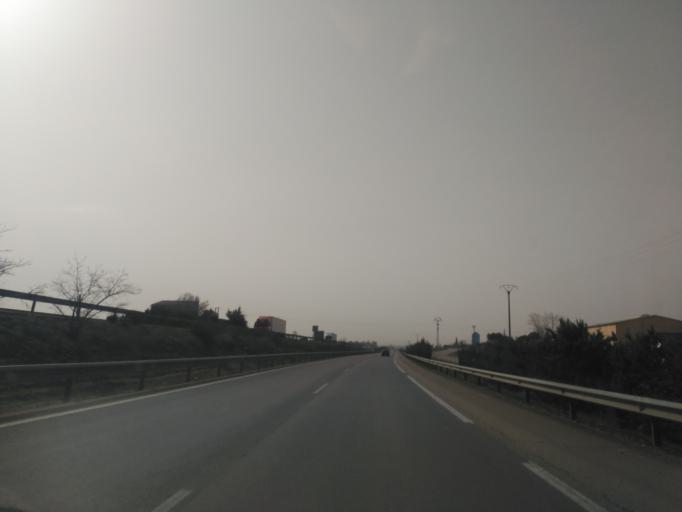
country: ES
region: Castille and Leon
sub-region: Provincia de Valladolid
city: Cubillas de Santa Marta
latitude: 41.8016
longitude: -4.5902
